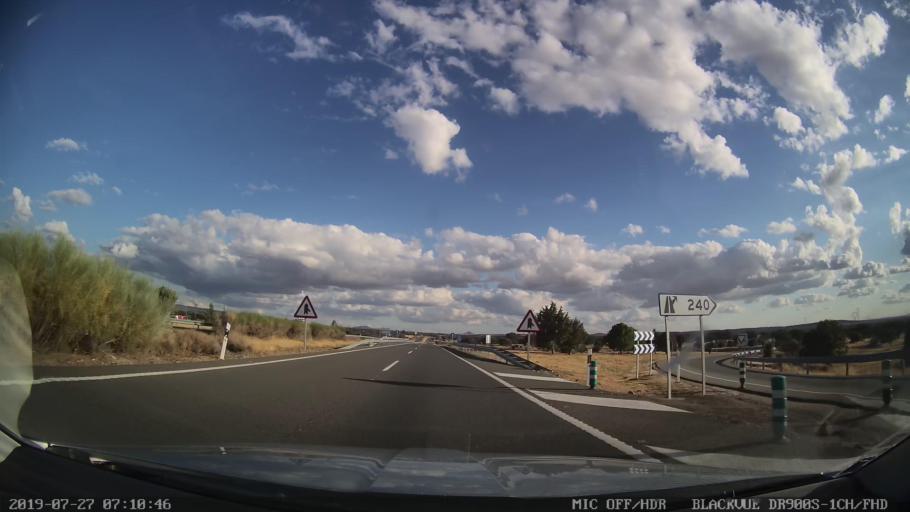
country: ES
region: Extremadura
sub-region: Provincia de Caceres
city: Torrecillas de la Tiesa
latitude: 39.5675
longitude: -5.8339
